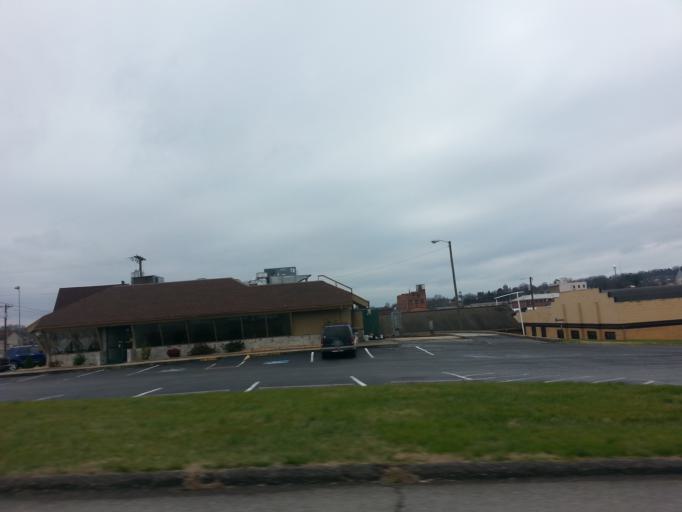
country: US
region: Tennessee
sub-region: Hamblen County
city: Morristown
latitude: 36.2144
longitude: -83.2876
